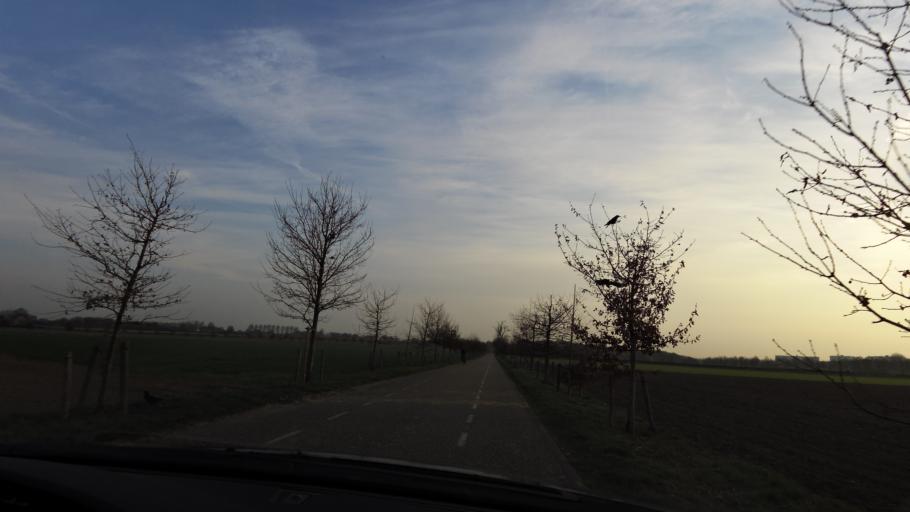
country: NL
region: Limburg
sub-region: Gemeente Schinnen
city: Amstenrade
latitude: 50.9429
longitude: 5.9326
